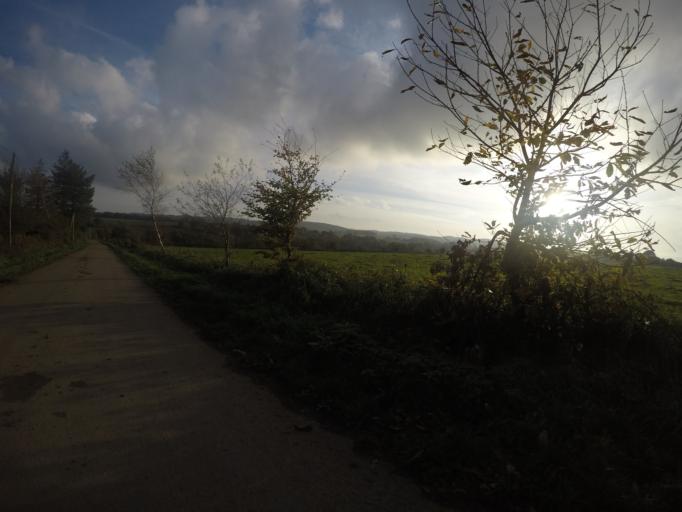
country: FR
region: Brittany
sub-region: Departement des Cotes-d'Armor
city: Bourbriac
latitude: 48.4673
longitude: -3.2929
